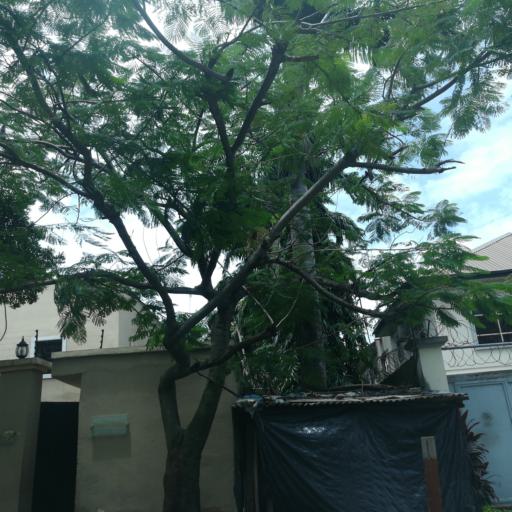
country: NG
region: Lagos
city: Ikoyi
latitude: 6.4395
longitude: 3.4660
